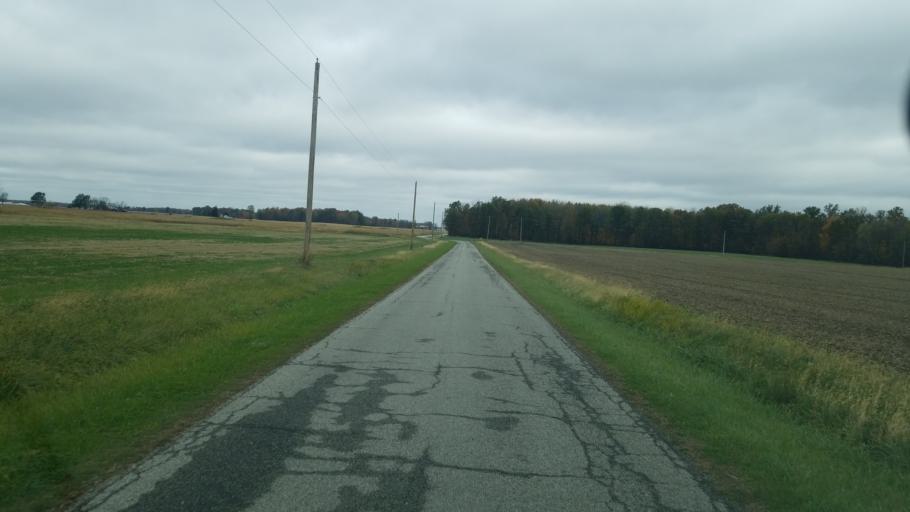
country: US
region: Ohio
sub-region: Crawford County
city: Bucyrus
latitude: 40.9046
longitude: -82.8825
